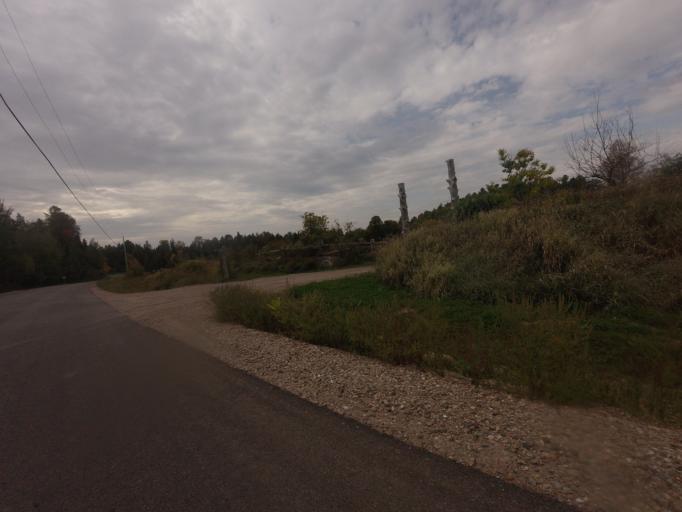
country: CA
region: Quebec
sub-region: Outaouais
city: Wakefield
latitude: 45.9884
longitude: -75.9458
